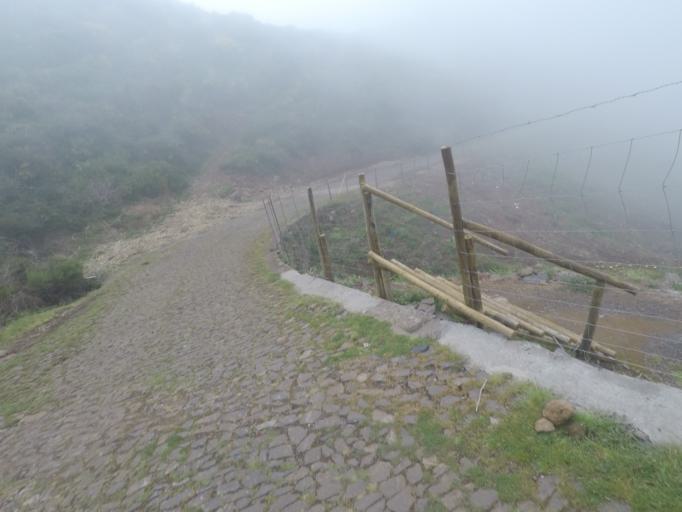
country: PT
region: Madeira
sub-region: Calheta
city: Arco da Calheta
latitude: 32.7355
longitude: -17.0969
